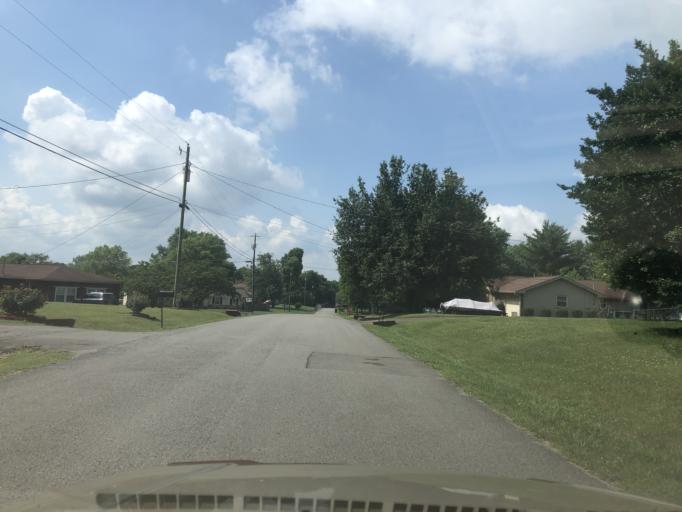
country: US
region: Tennessee
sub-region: Wilson County
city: Green Hill
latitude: 36.2369
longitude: -86.5889
